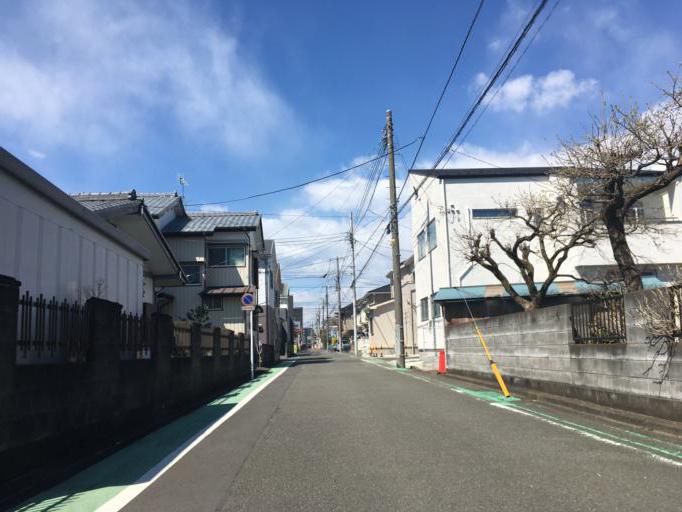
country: JP
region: Tokyo
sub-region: Machida-shi
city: Machida
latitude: 35.5721
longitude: 139.3827
